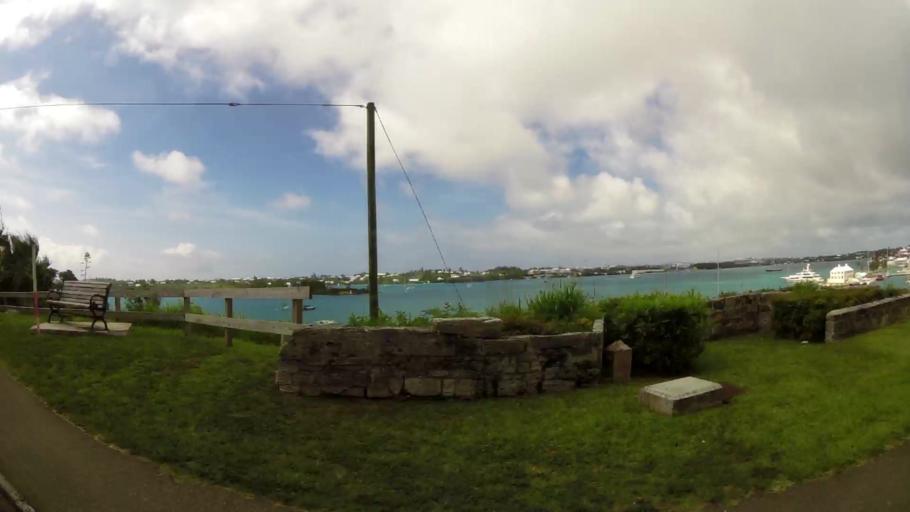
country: BM
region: Saint George
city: Saint George
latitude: 32.3820
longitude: -64.6726
